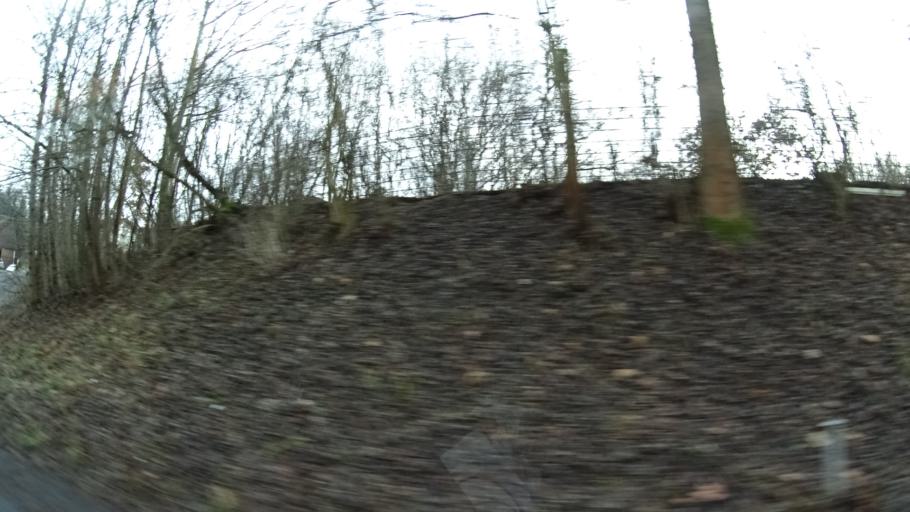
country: DE
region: Hesse
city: Tann
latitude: 50.6232
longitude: 10.0077
